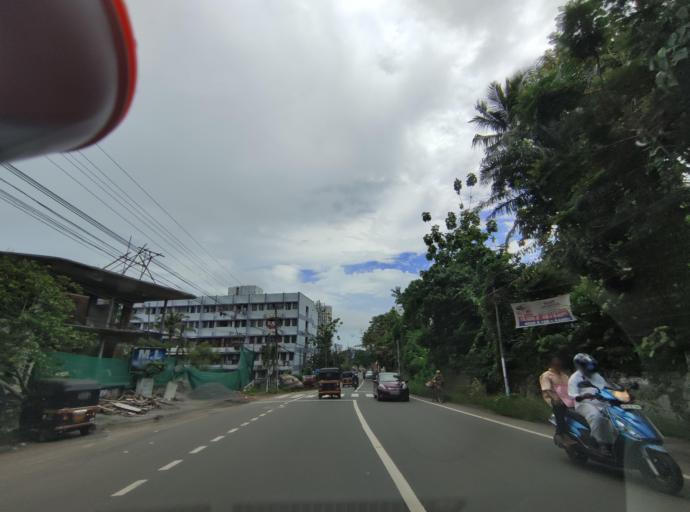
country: IN
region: Kerala
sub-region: Thiruvananthapuram
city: Thiruvananthapuram
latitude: 8.4930
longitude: 76.9699
